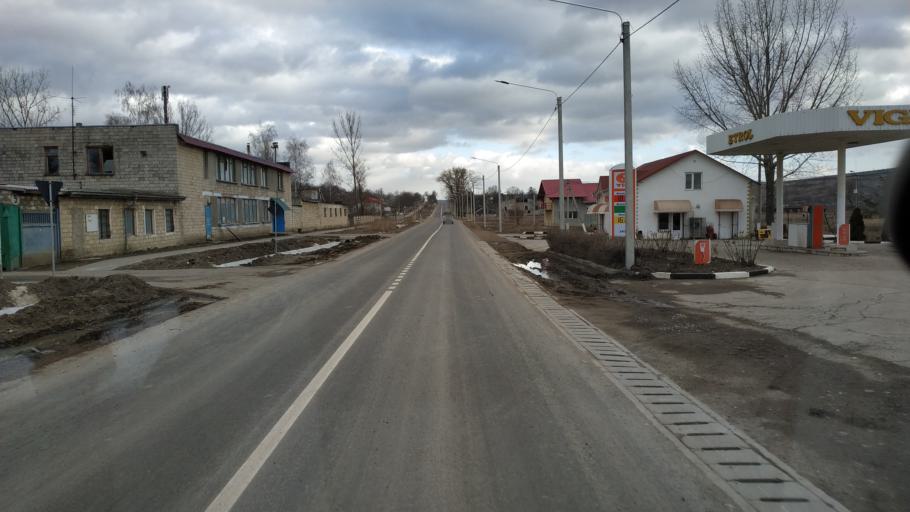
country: MD
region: Calarasi
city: Calarasi
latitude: 47.2806
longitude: 28.2085
